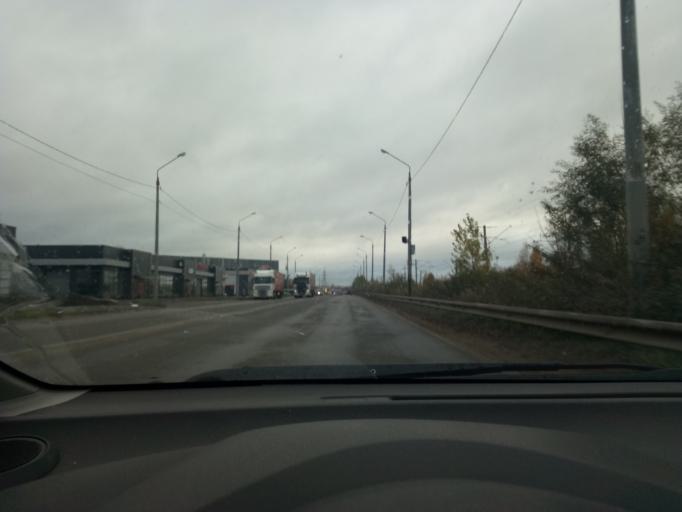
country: RU
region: Tatarstan
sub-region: Gorod Kazan'
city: Kazan
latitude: 55.8474
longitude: 49.1171
